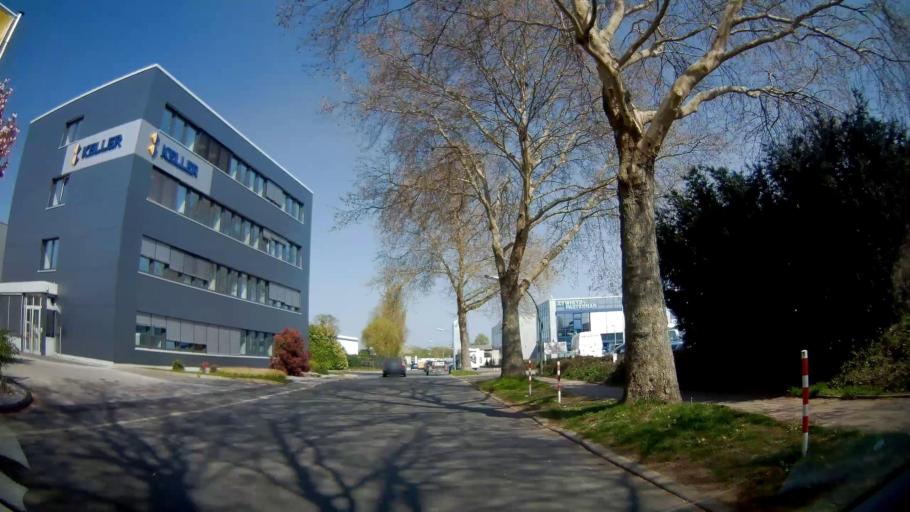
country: DE
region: North Rhine-Westphalia
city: Bochum-Hordel
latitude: 51.4833
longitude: 7.1620
